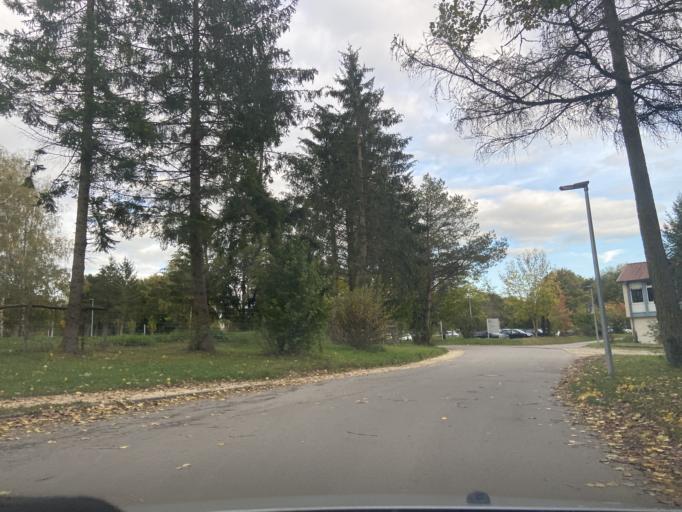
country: DE
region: Baden-Wuerttemberg
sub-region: Tuebingen Region
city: Sigmaringen
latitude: 48.0968
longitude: 9.2190
